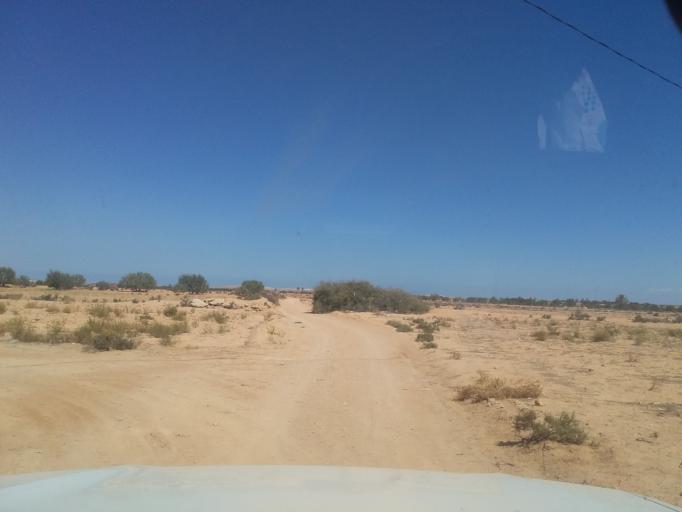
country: TN
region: Qabis
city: Matmata
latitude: 33.5152
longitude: 10.2196
